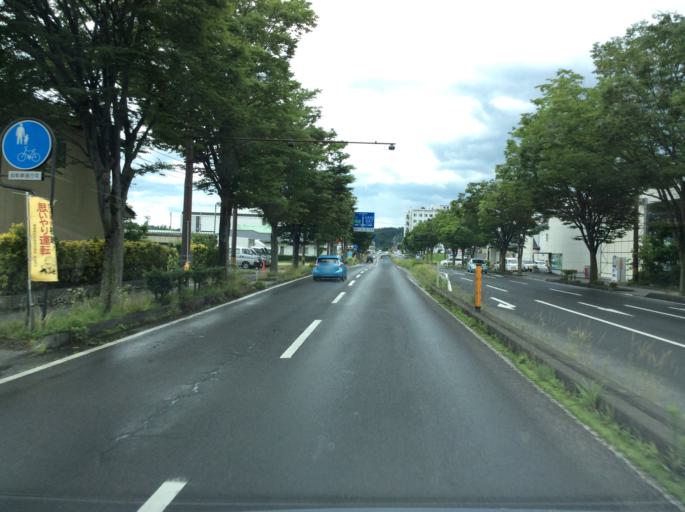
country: JP
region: Fukushima
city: Fukushima-shi
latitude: 37.7298
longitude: 140.3870
